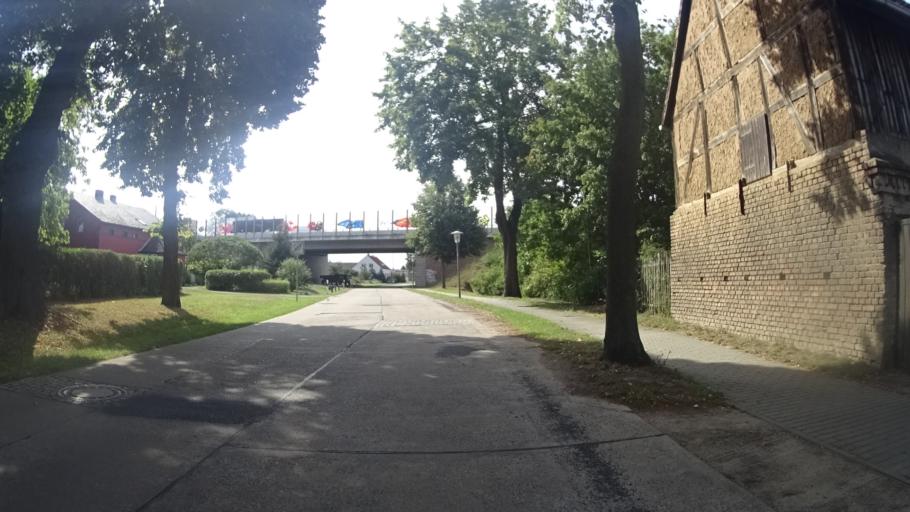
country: DE
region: Brandenburg
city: Golzow
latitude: 52.3361
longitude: 12.6611
